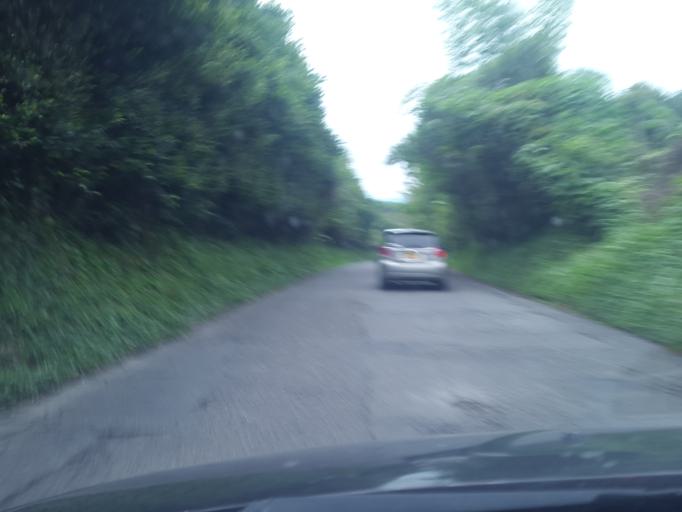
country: CO
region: Quindio
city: La Tebaida
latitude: 4.5018
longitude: -75.7945
